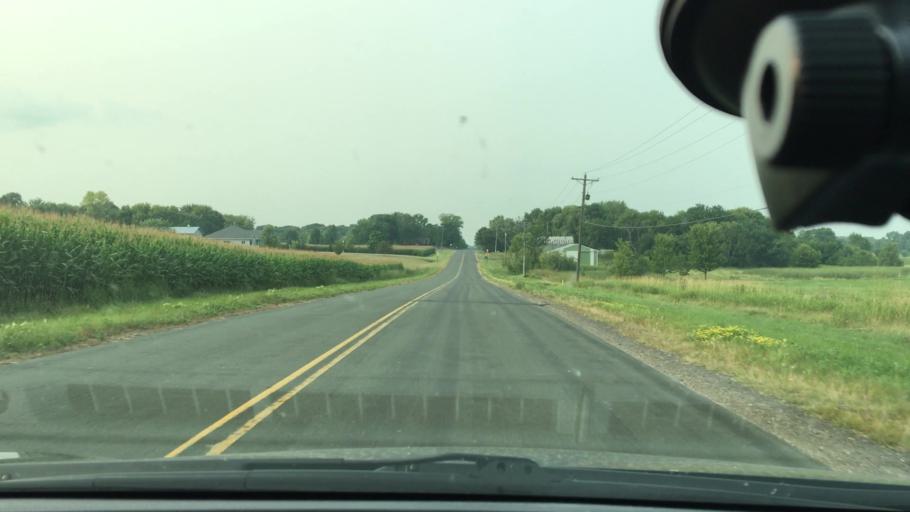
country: US
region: Minnesota
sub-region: Wright County
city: Albertville
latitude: 45.2866
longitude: -93.6839
